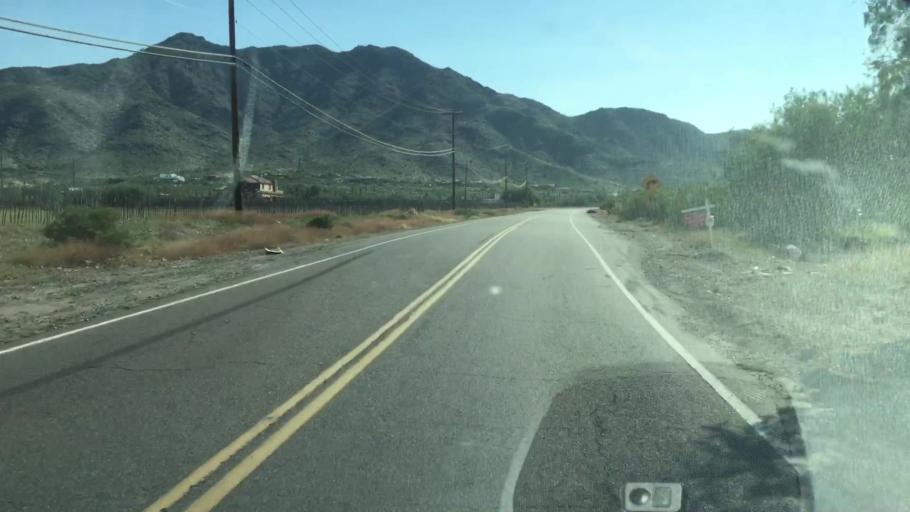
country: US
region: Arizona
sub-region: Maricopa County
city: Laveen
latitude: 33.3512
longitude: -112.1349
